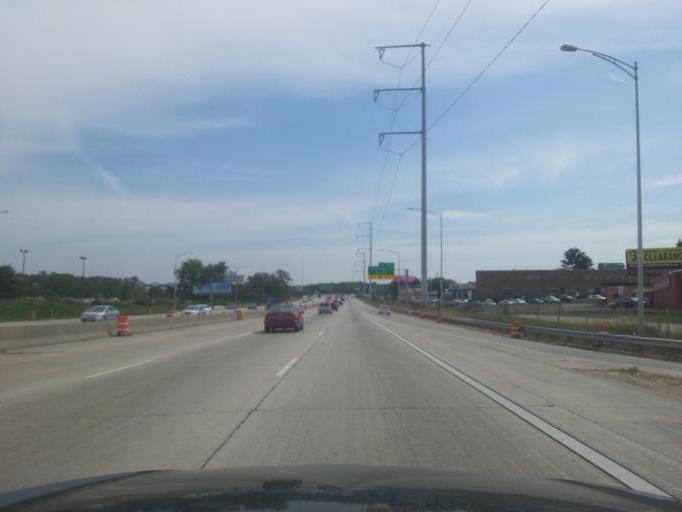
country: US
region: Wisconsin
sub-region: Dane County
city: Madison
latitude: 43.0408
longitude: -89.3768
